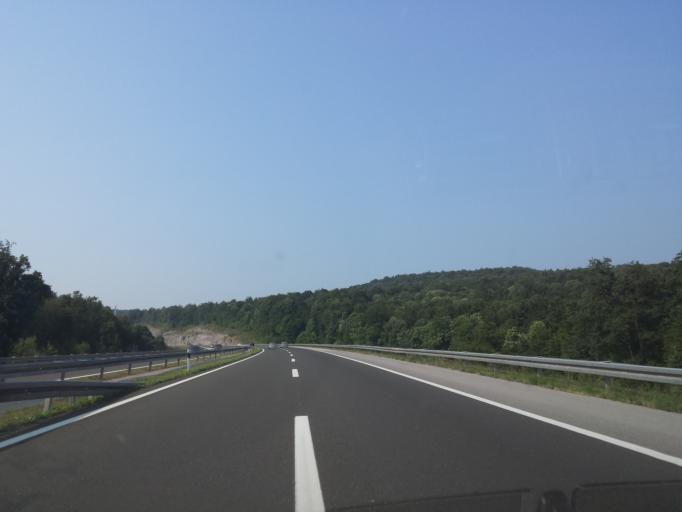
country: HR
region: Karlovacka
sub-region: Grad Ogulin
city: Ogulin
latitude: 45.2745
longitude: 15.2721
